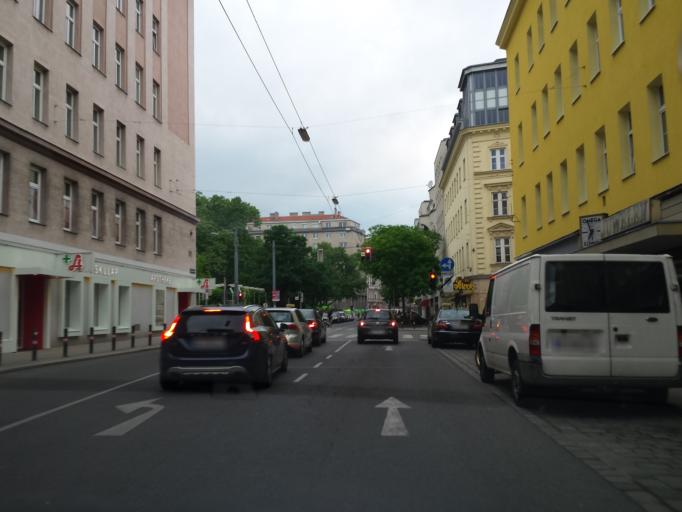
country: AT
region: Vienna
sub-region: Wien Stadt
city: Vienna
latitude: 48.1972
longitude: 16.4030
